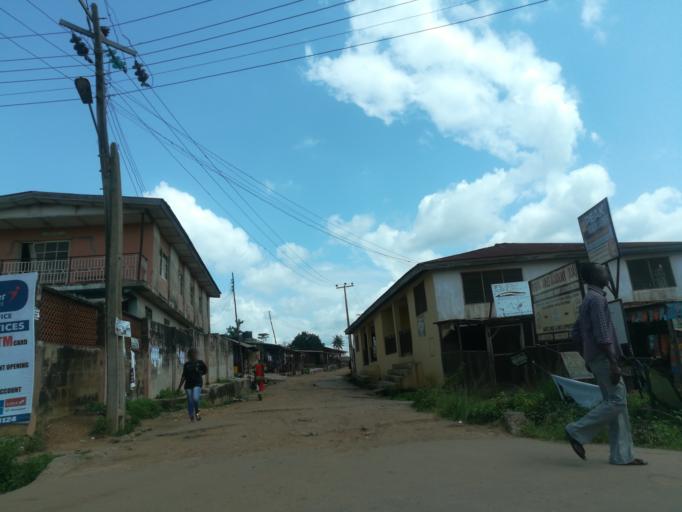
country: NG
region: Oyo
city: Egbeda
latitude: 7.4303
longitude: 4.0058
